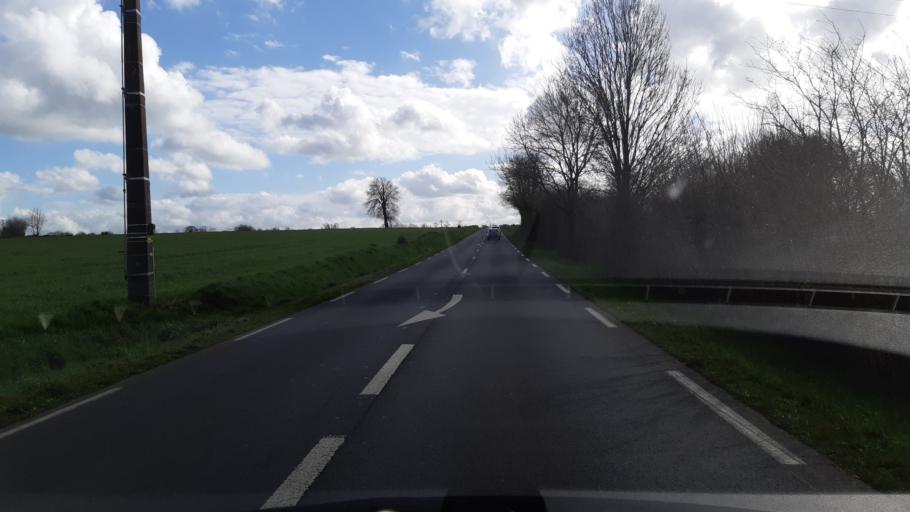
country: FR
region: Lower Normandy
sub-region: Departement de la Manche
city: Agneaux
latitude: 49.0431
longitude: -1.1293
